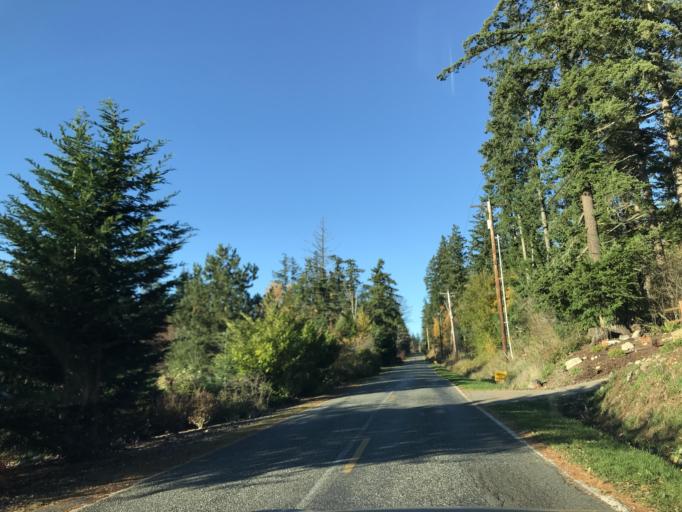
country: US
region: Washington
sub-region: Whatcom County
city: Geneva
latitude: 48.7720
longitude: -122.3991
